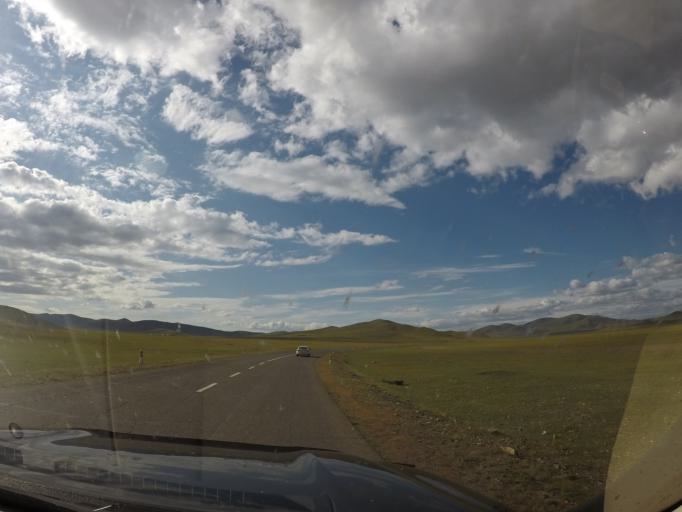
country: MN
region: Hentiy
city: Modot
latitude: 47.6608
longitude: 109.1287
